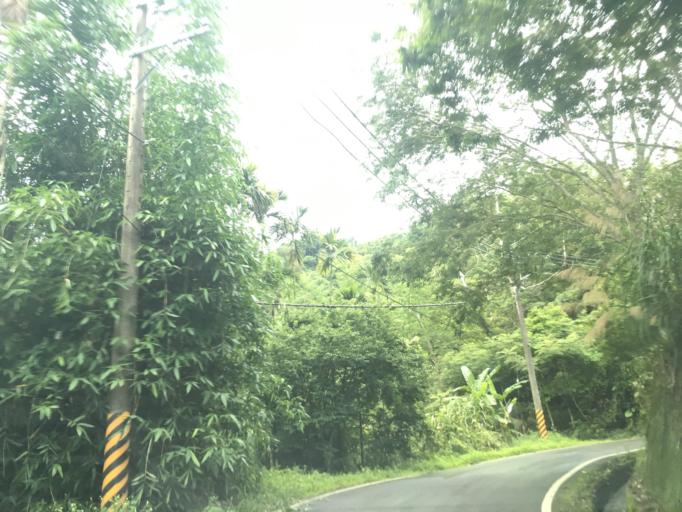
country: TW
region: Taiwan
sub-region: Yunlin
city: Douliu
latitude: 23.5647
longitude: 120.6469
